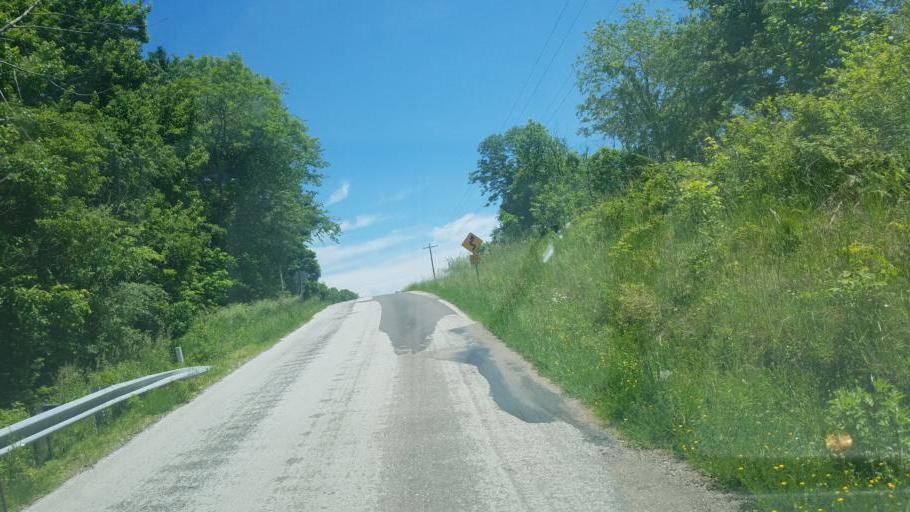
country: US
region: Ohio
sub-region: Coshocton County
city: Coshocton
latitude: 40.2687
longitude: -81.9265
